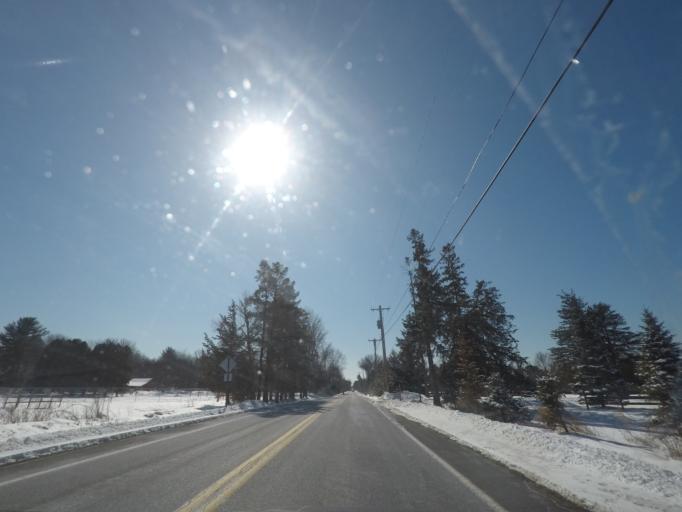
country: US
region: New York
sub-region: Saratoga County
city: Ballston Spa
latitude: 42.9849
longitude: -73.8331
